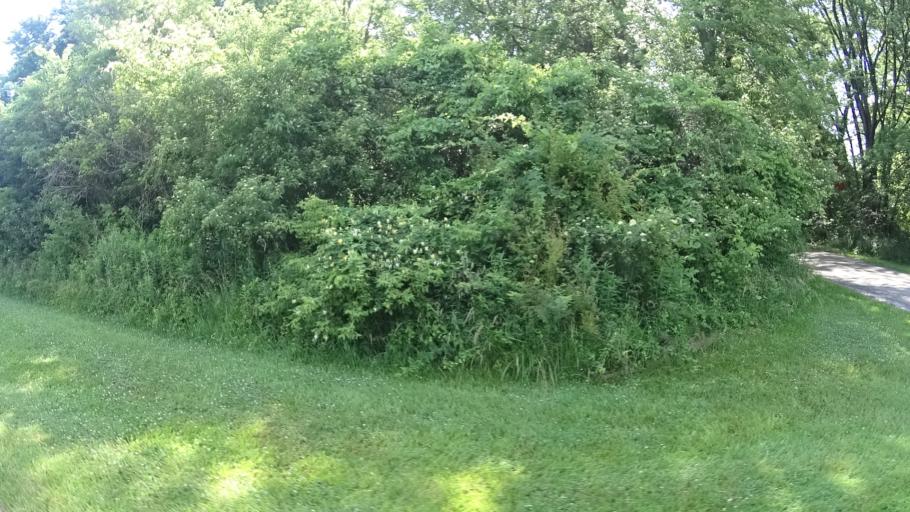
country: US
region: Ohio
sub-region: Erie County
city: Huron
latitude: 41.3792
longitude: -82.5072
